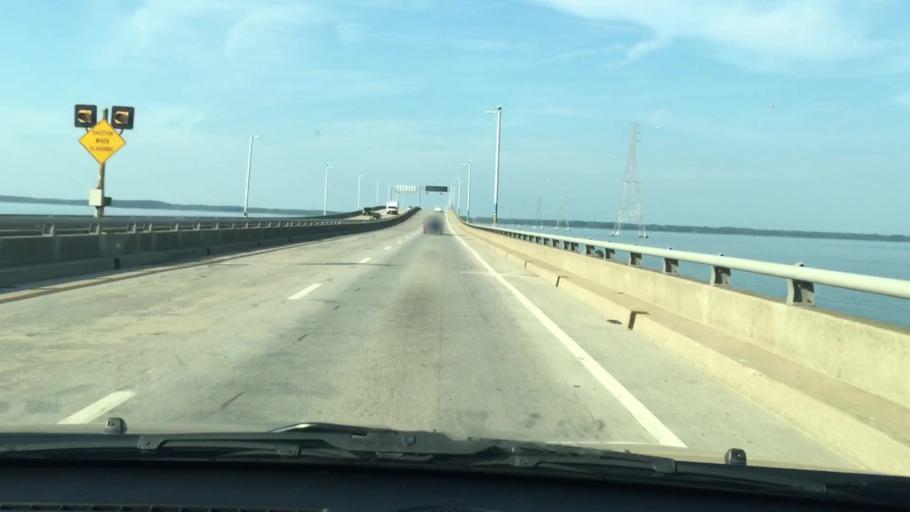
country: US
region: Virginia
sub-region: City of Newport News
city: Newport News
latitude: 36.9947
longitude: -76.4789
